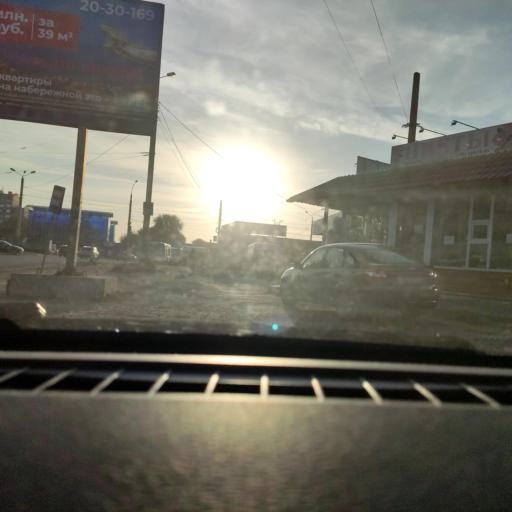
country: RU
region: Voronezj
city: Maslovka
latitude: 51.5993
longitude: 39.2483
